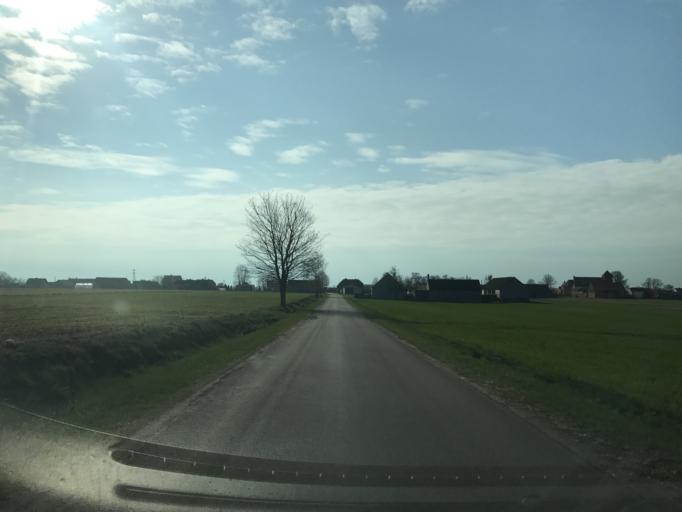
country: PL
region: Warmian-Masurian Voivodeship
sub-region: Powiat dzialdowski
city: Lidzbark
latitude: 53.3113
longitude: 19.8586
